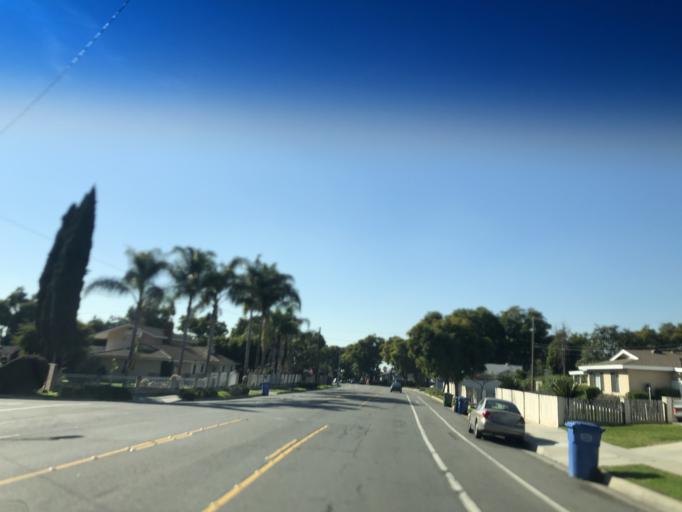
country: US
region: California
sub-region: Los Angeles County
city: South Whittier
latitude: 33.9481
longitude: -118.0149
